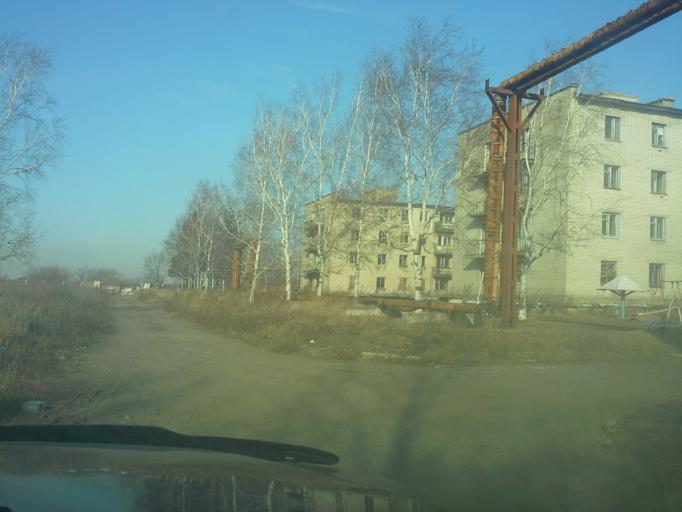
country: RU
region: Jewish Autonomous Oblast
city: Priamurskiy
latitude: 48.3598
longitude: 134.7958
